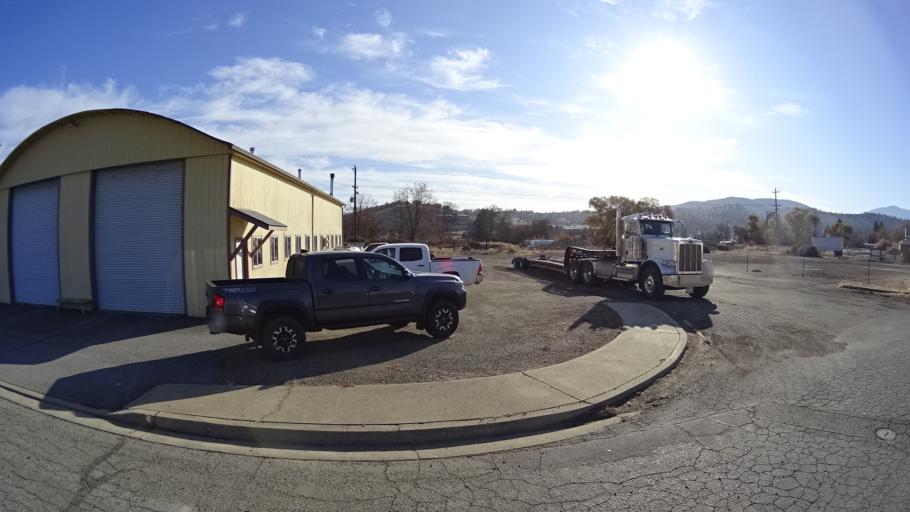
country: US
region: California
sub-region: Siskiyou County
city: Yreka
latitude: 41.7136
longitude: -122.6384
